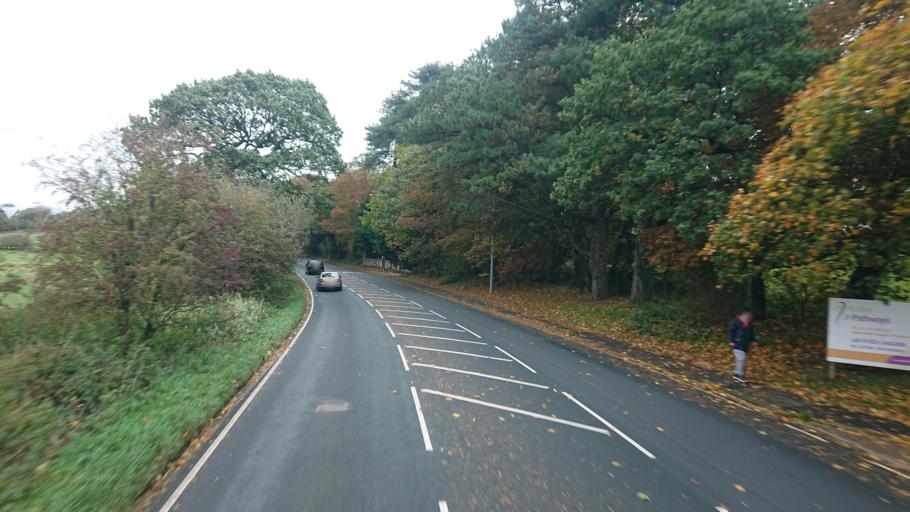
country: GB
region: England
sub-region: Lancashire
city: Lancaster
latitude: 54.0203
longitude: -2.7957
